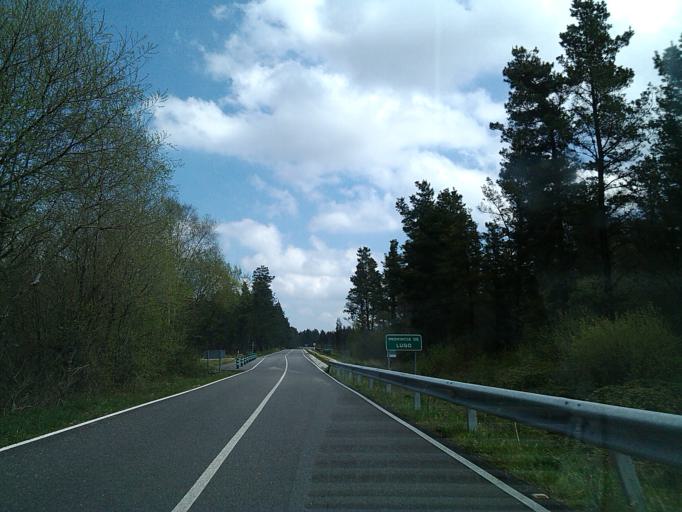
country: ES
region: Galicia
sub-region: Provincia da Coruna
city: Sobrado
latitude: 43.0324
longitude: -7.9258
